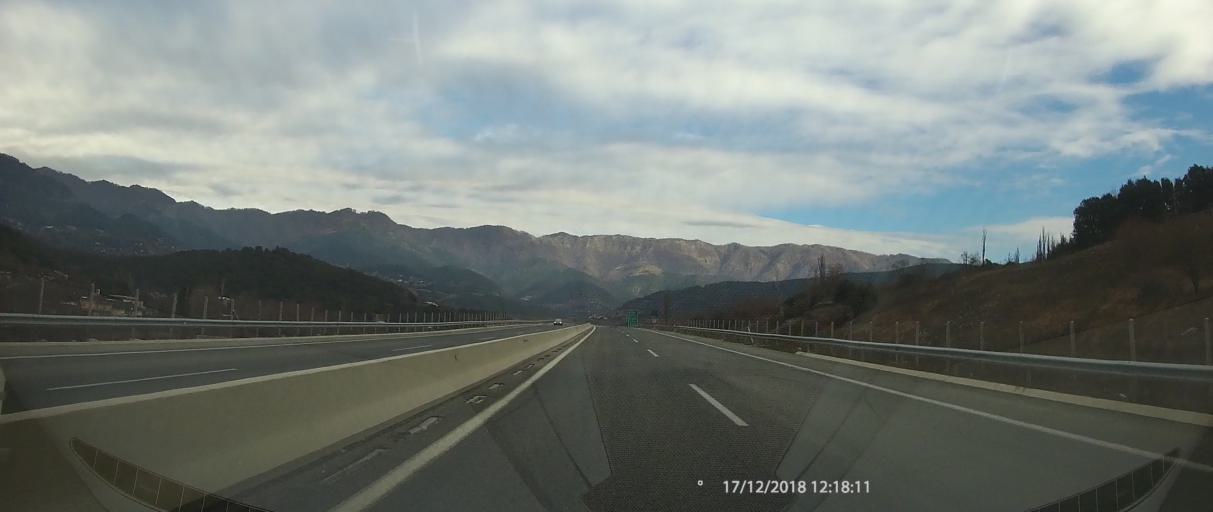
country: GR
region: Epirus
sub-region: Nomos Ioanninon
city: Metsovo
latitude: 39.7501
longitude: 21.0780
